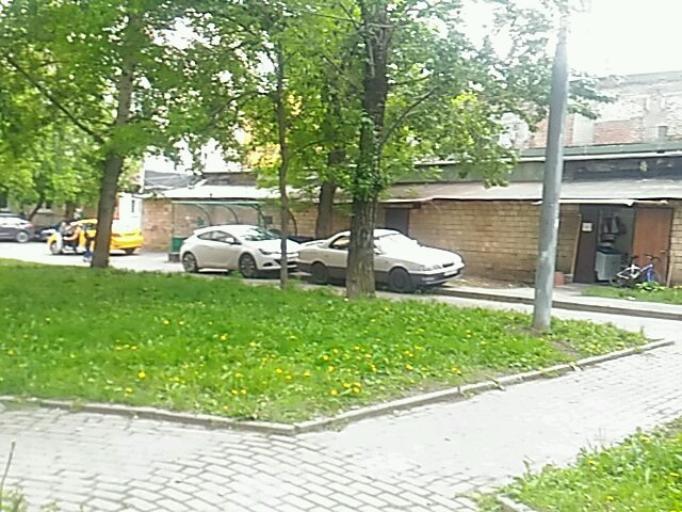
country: RU
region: Moskovskaya
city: Presnenskiy
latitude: 55.7623
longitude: 37.5388
